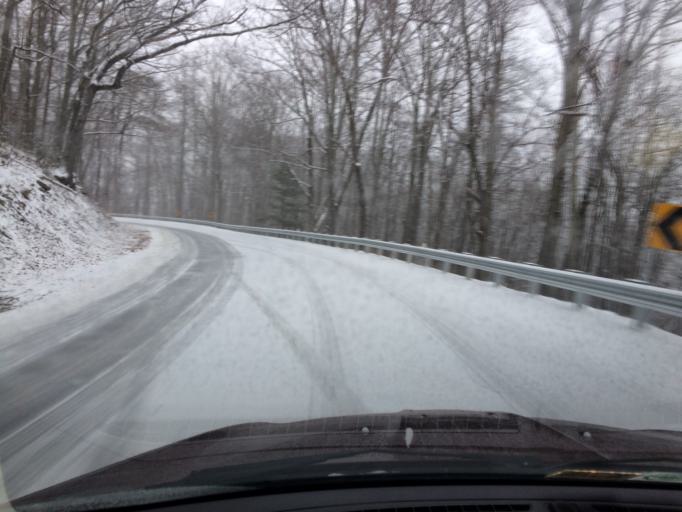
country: US
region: Virginia
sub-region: City of Buena Vista
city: Buena Vista
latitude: 37.7476
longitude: -79.2902
